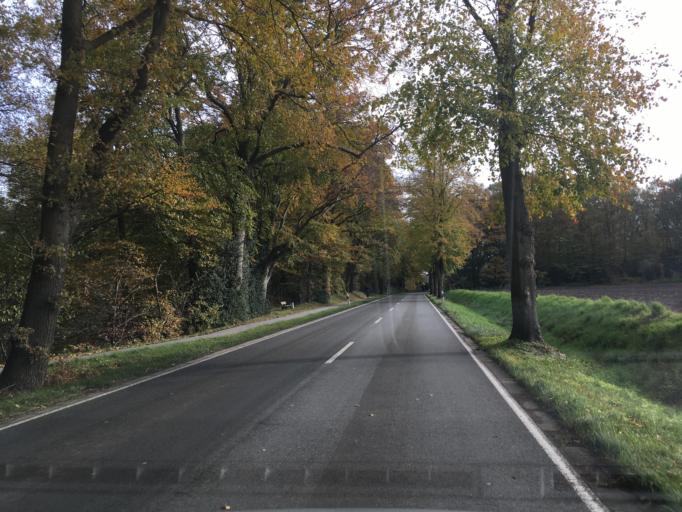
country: DE
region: North Rhine-Westphalia
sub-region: Regierungsbezirk Munster
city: Klein Reken
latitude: 51.8448
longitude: 7.0864
